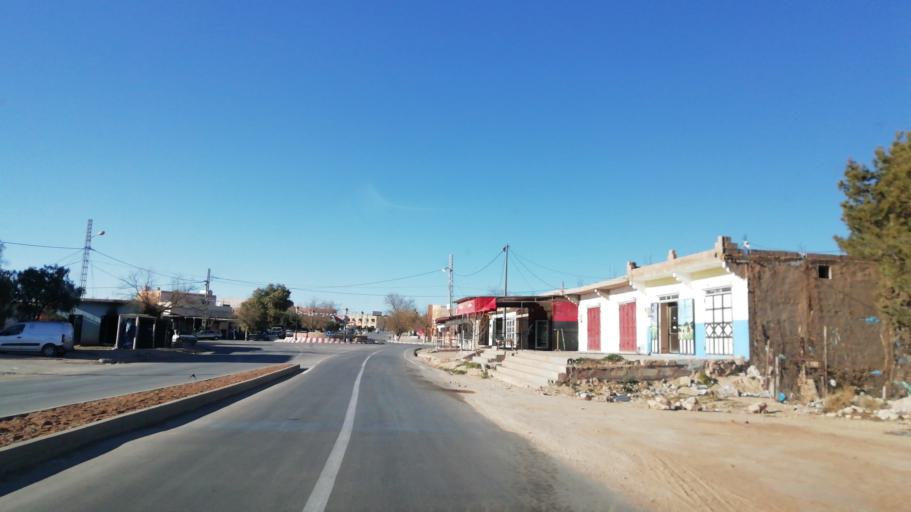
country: DZ
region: Tlemcen
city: Sebdou
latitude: 34.2238
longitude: -1.2527
